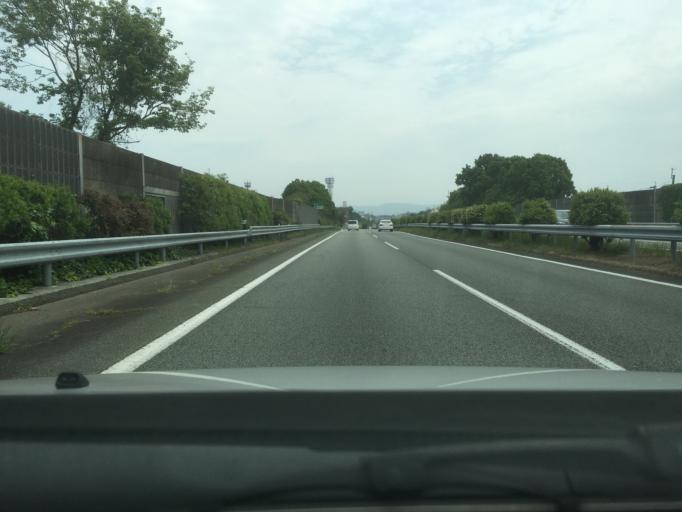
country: JP
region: Kumamoto
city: Kumamoto
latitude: 32.8515
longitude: 130.7639
